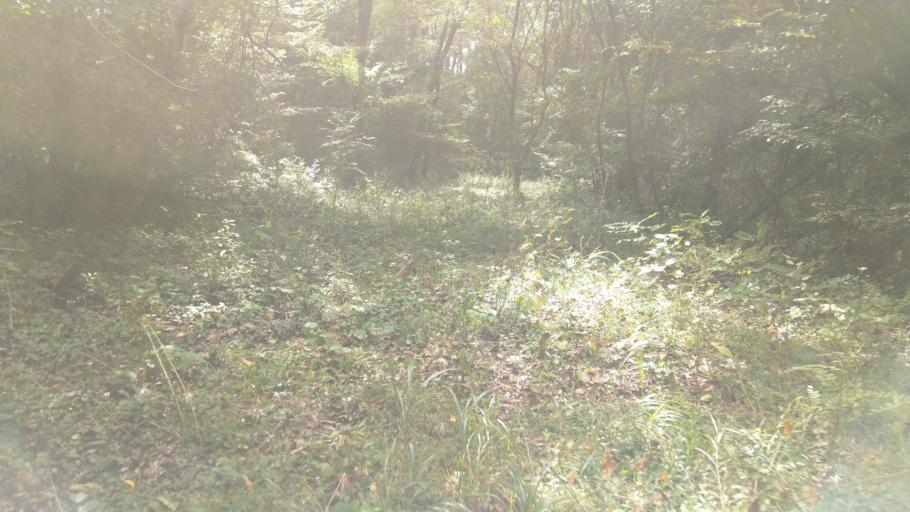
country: JP
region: Nagano
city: Komoro
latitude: 36.3402
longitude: 138.4317
